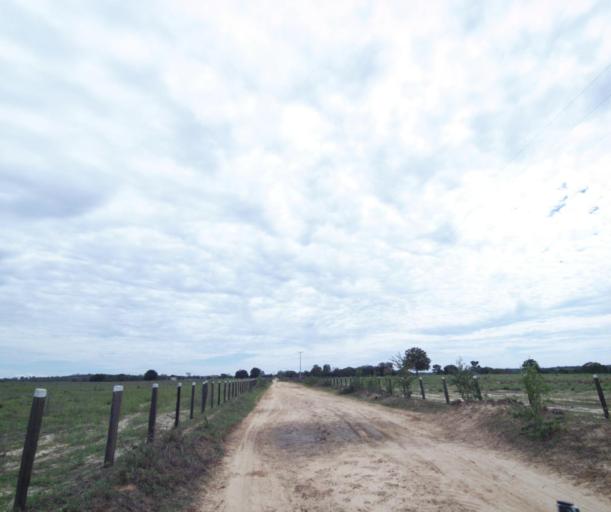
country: BR
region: Bahia
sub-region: Carinhanha
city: Carinhanha
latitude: -14.2541
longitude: -44.3565
